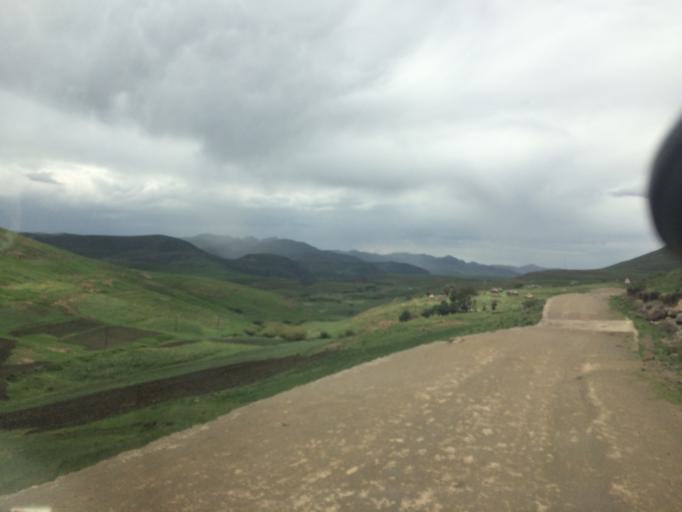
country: LS
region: Maseru
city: Nako
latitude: -29.8486
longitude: 28.0279
